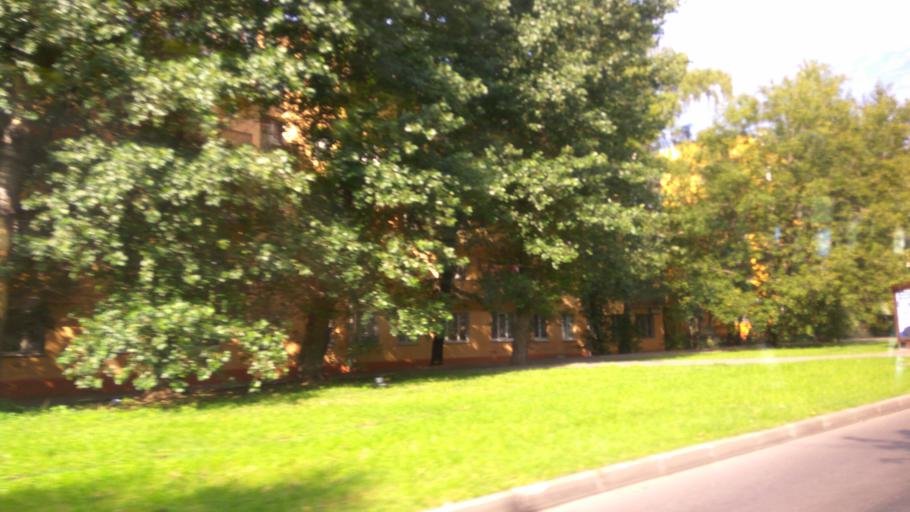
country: RU
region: Moscow
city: Lefortovo
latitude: 55.7651
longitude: 37.7395
